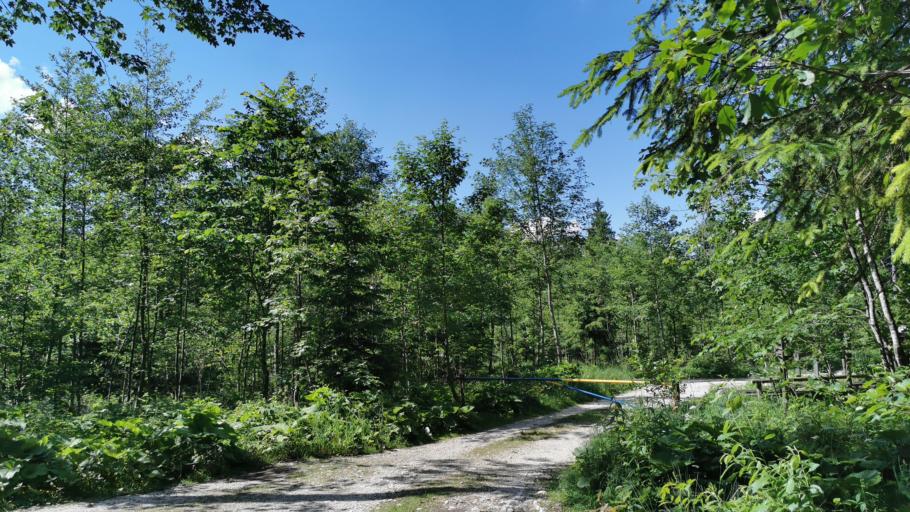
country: DE
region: Bavaria
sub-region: Upper Bavaria
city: Piding
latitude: 47.7396
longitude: 12.9616
